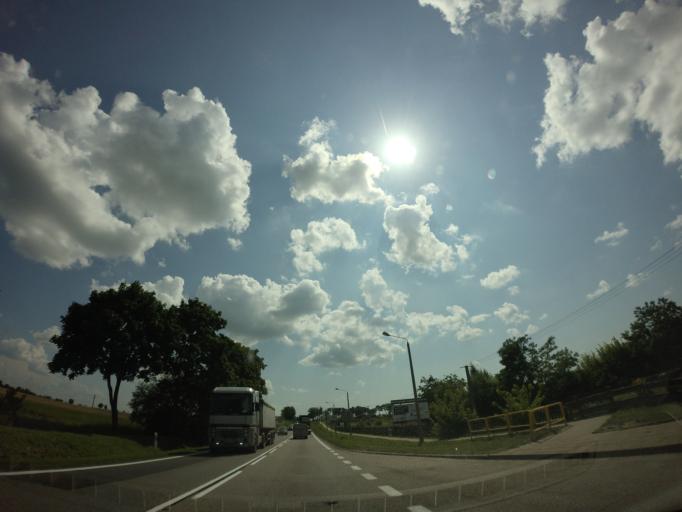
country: PL
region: Podlasie
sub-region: Powiat lomzynski
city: Piatnica
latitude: 53.2511
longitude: 22.1205
